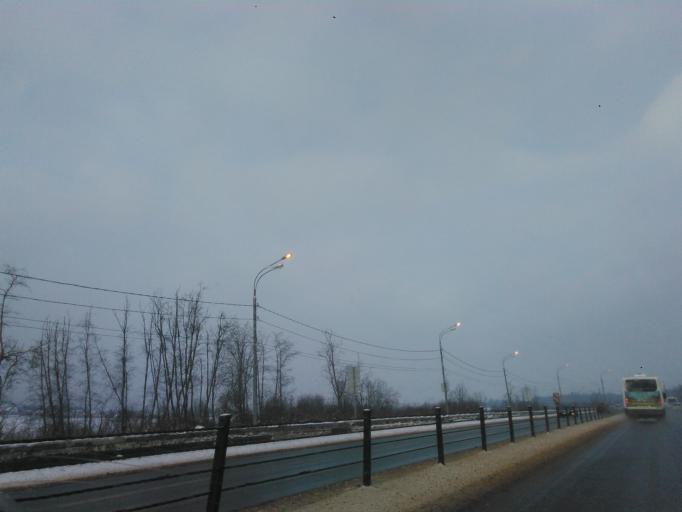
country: RU
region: Moskovskaya
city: Dedenevo
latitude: 56.2164
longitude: 37.5216
